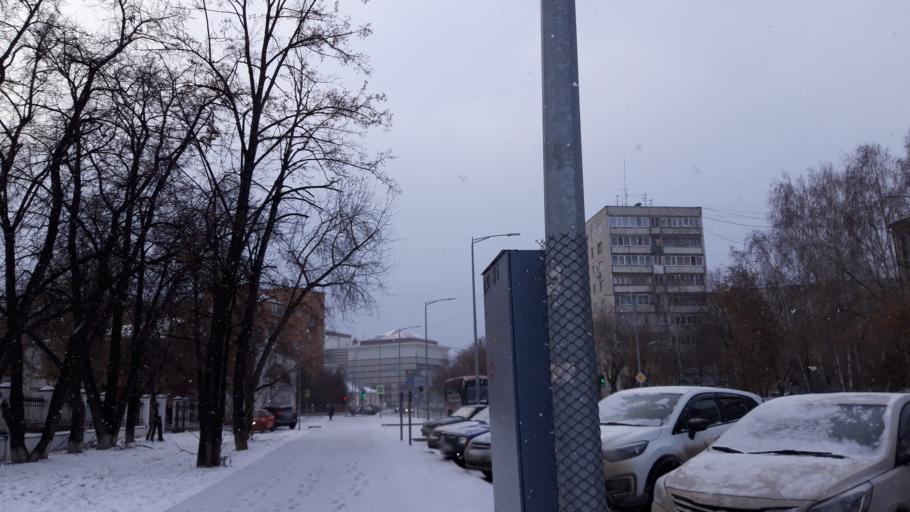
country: RU
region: Tjumen
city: Tyumen
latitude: 57.1567
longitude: 65.5513
